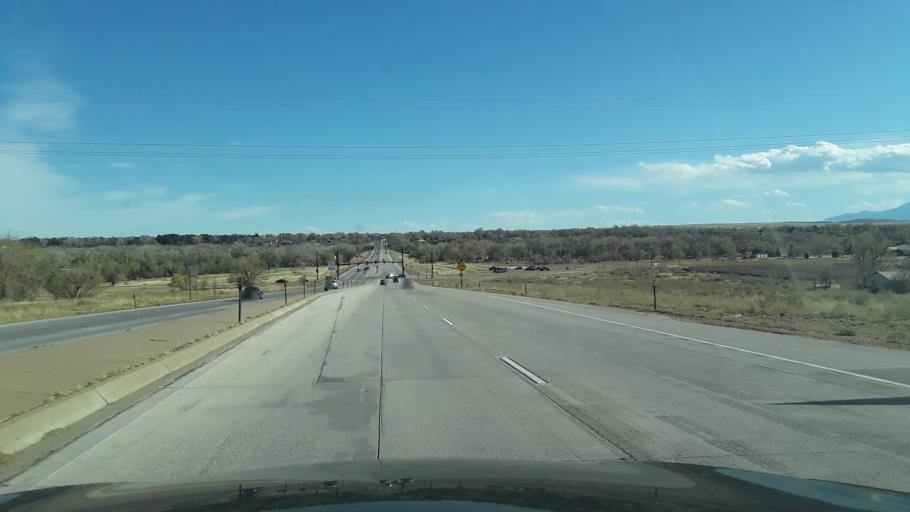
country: US
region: Colorado
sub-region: Pueblo County
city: Pueblo
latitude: 38.2796
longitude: -104.6631
